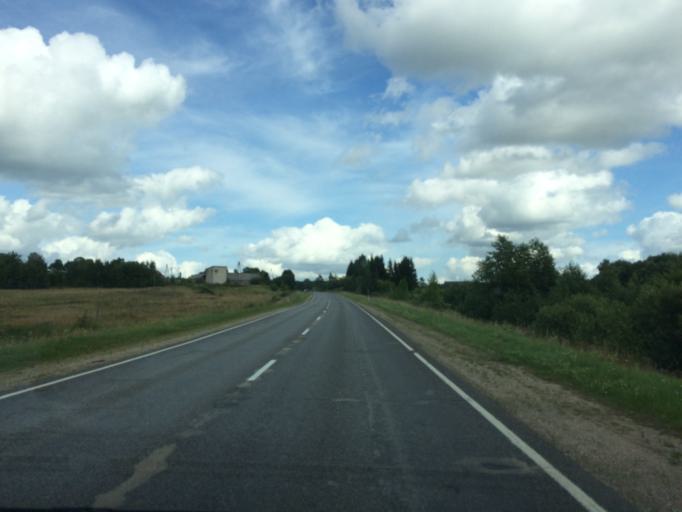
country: LV
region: Rezekne
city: Rezekne
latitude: 56.6108
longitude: 27.4424
